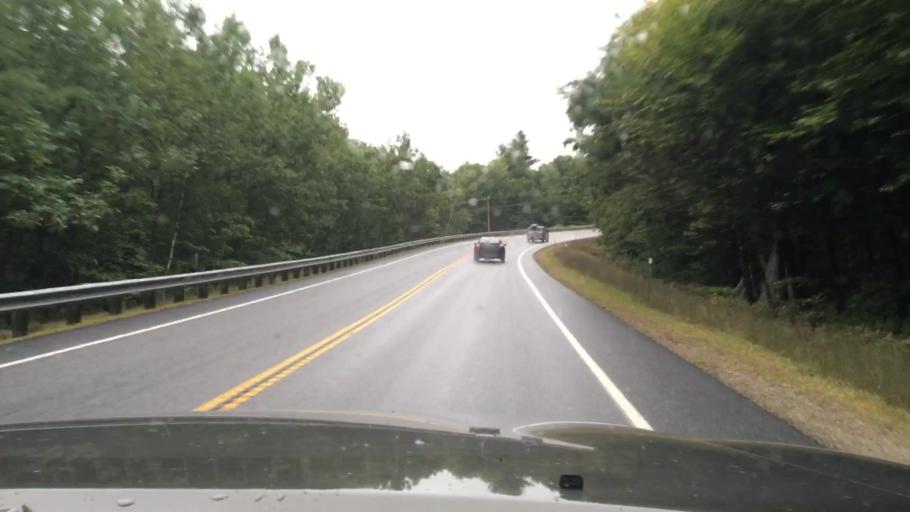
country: US
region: New Hampshire
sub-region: Hillsborough County
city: Antrim
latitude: 43.0676
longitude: -72.0548
